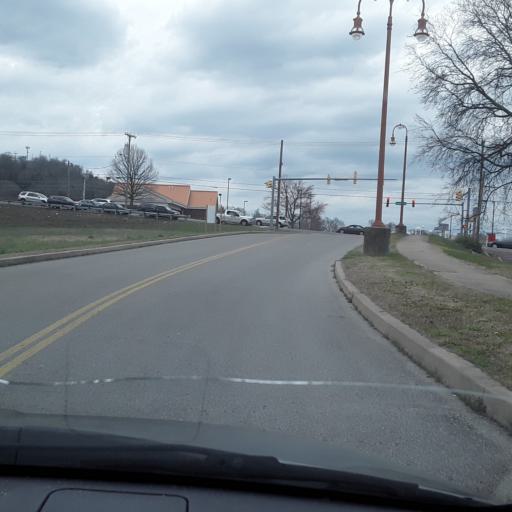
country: US
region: Tennessee
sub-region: Davidson County
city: Lakewood
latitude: 36.1678
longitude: -86.6672
